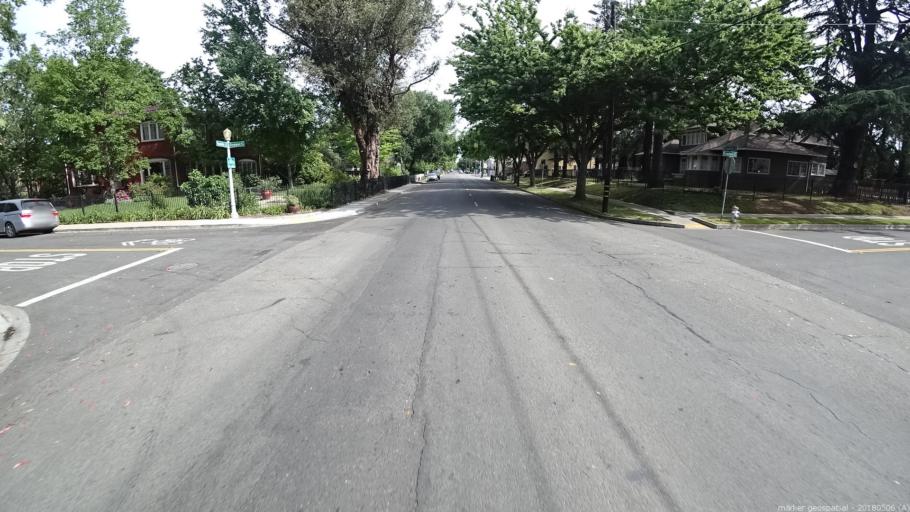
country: US
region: California
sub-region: Sacramento County
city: Sacramento
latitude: 38.5481
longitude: -121.4759
